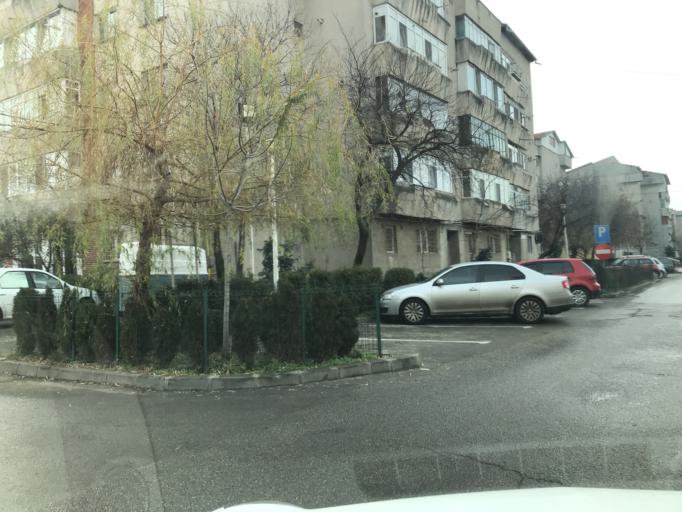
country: RO
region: Olt
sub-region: Municipiul Slatina
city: Slatina
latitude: 44.4289
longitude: 24.3852
